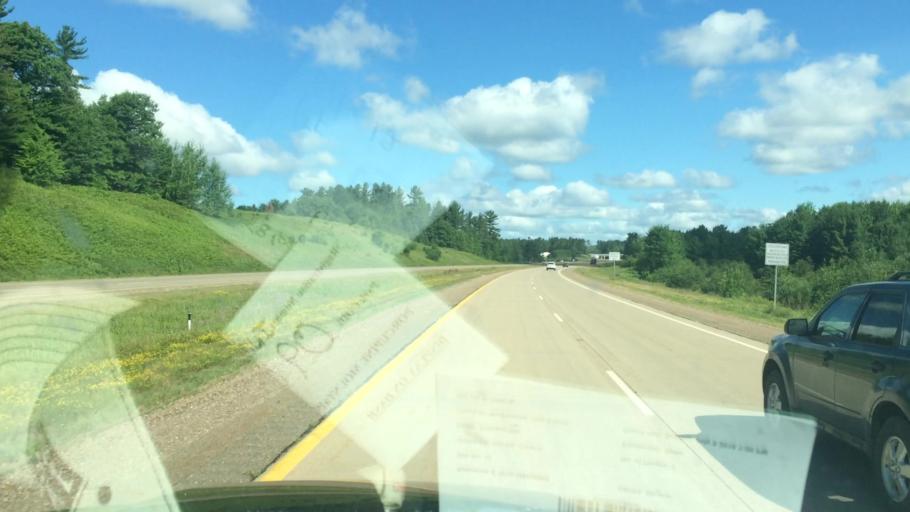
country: US
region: Wisconsin
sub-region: Lincoln County
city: Tomahawk
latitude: 45.4270
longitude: -89.6769
